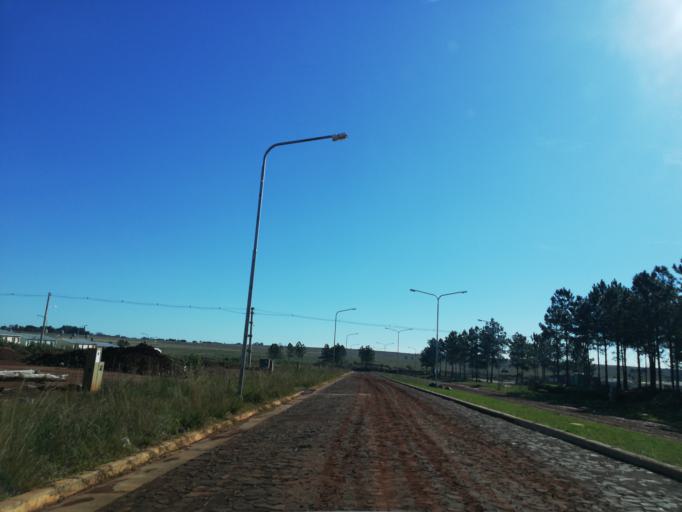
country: AR
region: Misiones
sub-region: Departamento de Capital
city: Posadas
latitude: -27.4064
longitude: -55.9935
